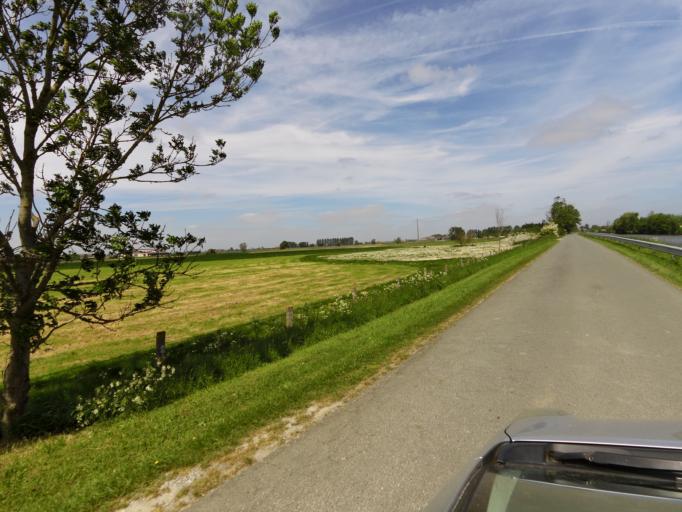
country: BE
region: Flanders
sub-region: Provincie West-Vlaanderen
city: Diksmuide
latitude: 50.9986
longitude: 2.8254
